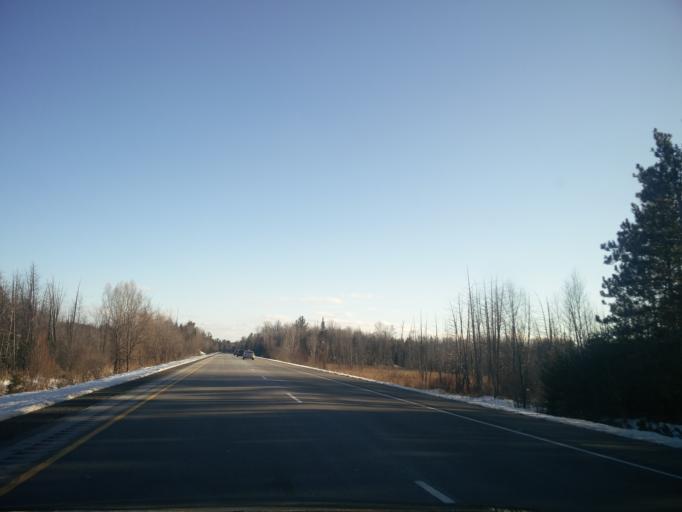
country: CA
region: Ontario
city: Prescott
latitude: 44.8023
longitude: -75.5147
